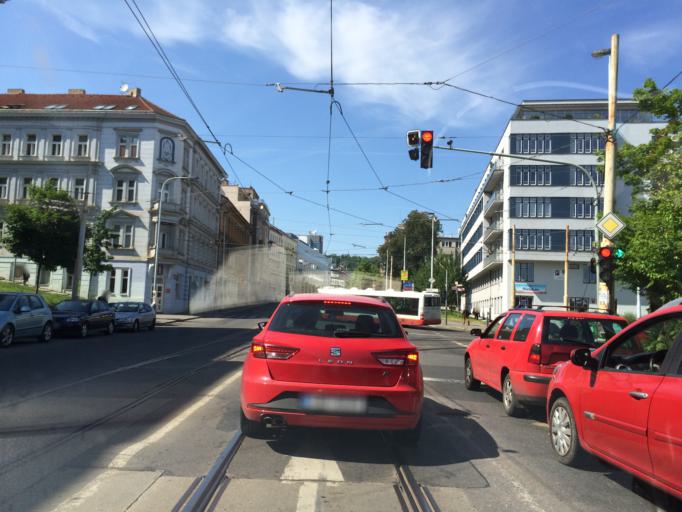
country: CZ
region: Praha
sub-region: Praha 2
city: Vysehrad
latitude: 50.0676
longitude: 14.4024
